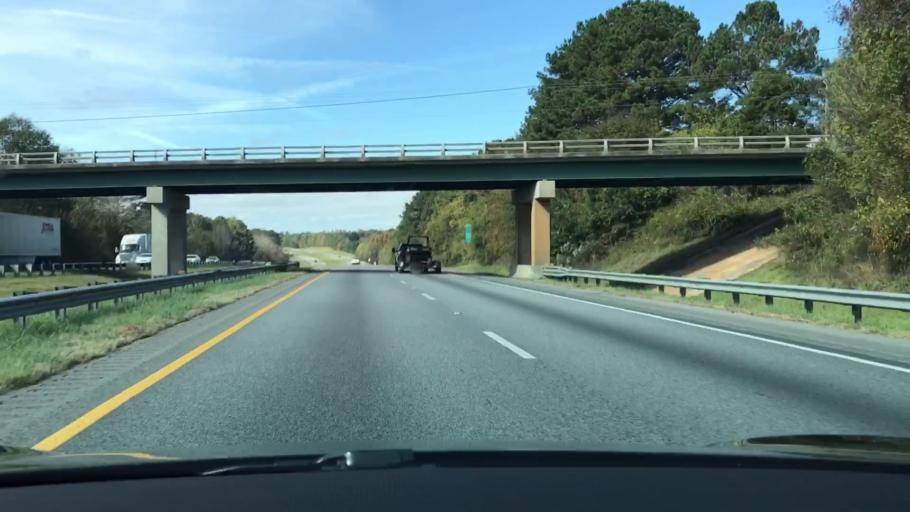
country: US
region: Georgia
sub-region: Walton County
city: Social Circle
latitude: 33.6002
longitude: -83.6515
